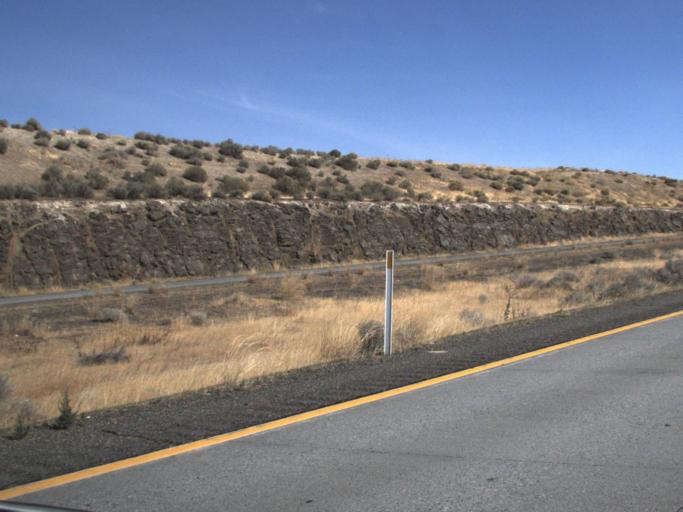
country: US
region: Washington
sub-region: Franklin County
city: West Pasco
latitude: 46.1849
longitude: -119.2497
